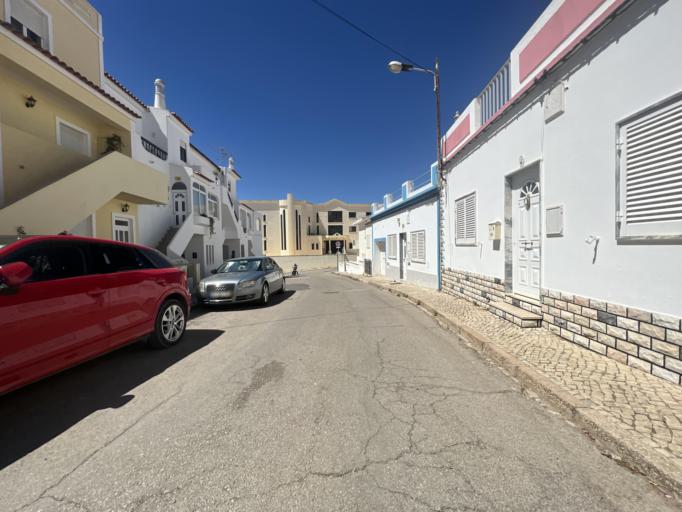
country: PT
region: Faro
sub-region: Portimao
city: Portimao
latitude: 37.1231
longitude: -8.5207
